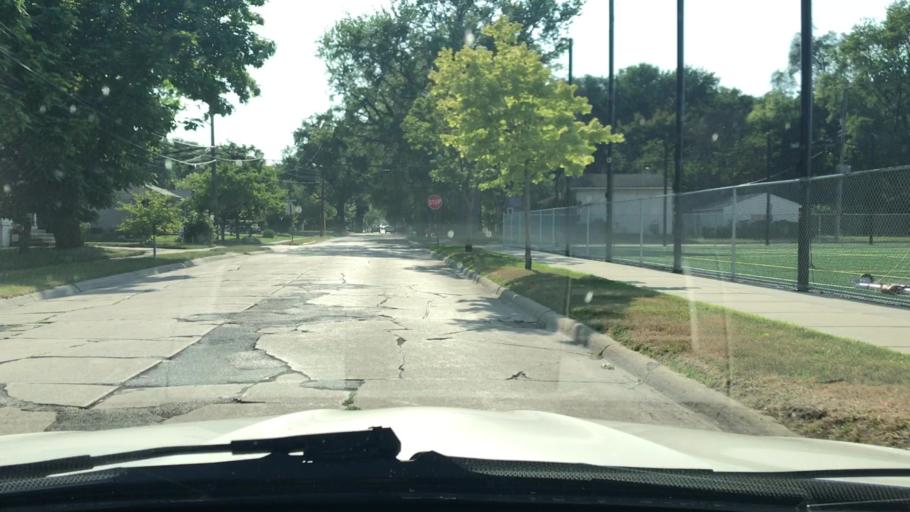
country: US
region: Michigan
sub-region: Oakland County
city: Clawson
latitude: 42.5347
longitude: -83.1491
